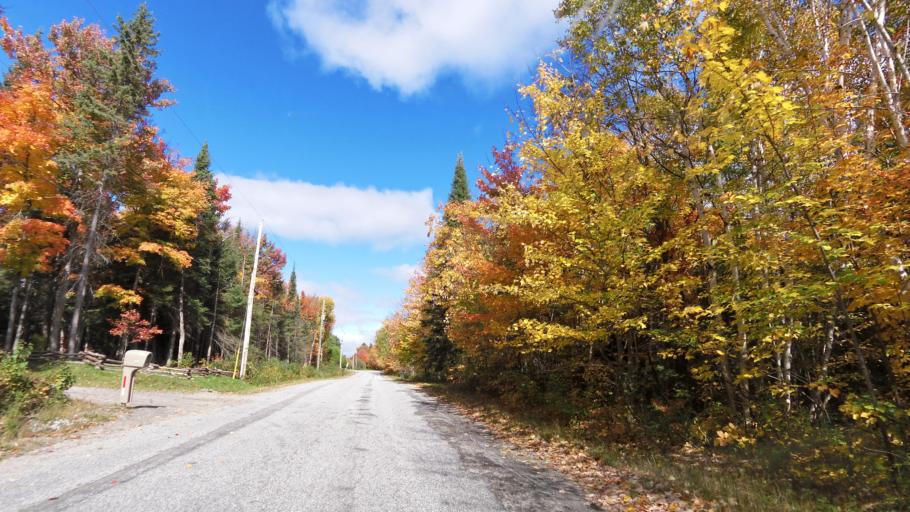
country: CA
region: Ontario
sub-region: Nipissing District
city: North Bay
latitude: 46.3743
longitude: -79.4871
